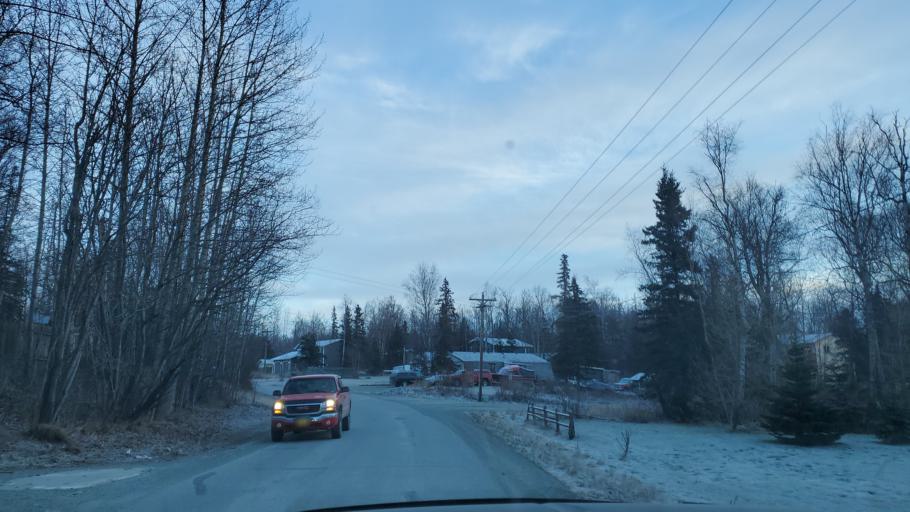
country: US
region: Alaska
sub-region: Matanuska-Susitna Borough
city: Lakes
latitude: 61.6083
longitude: -149.3122
